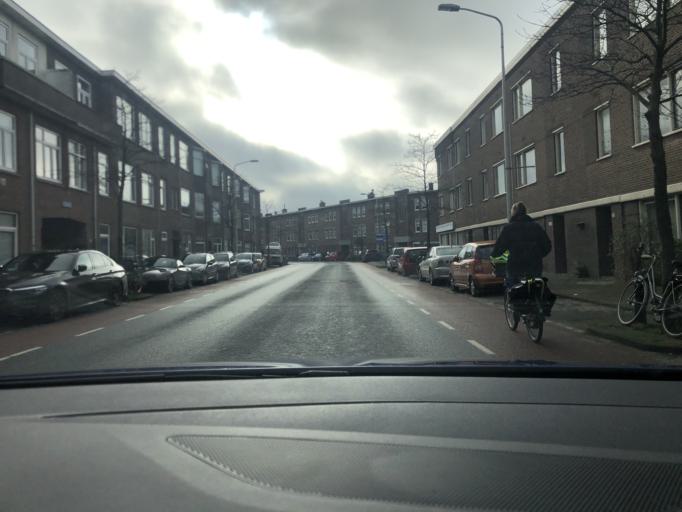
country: NL
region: South Holland
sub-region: Gemeente Den Haag
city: The Hague
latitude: 52.0719
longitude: 4.2675
